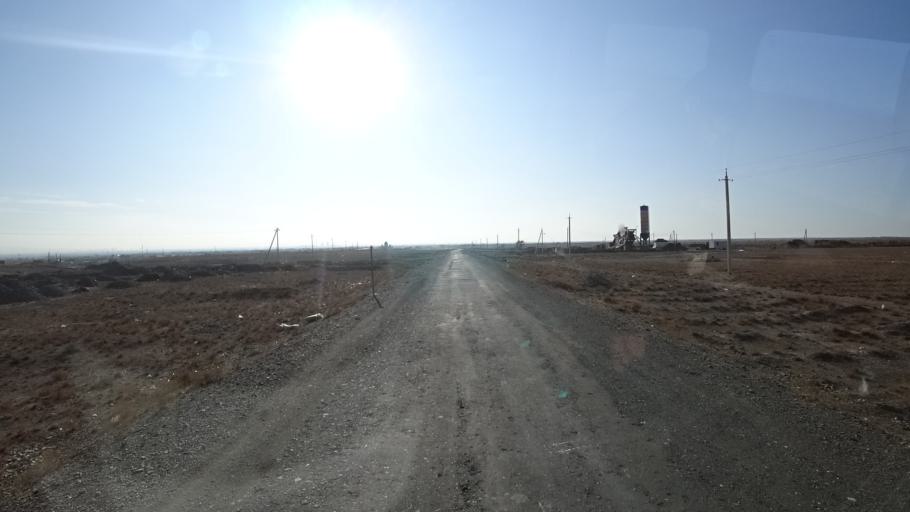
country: UZ
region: Navoiy
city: Beshrabot
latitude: 40.2234
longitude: 65.3935
